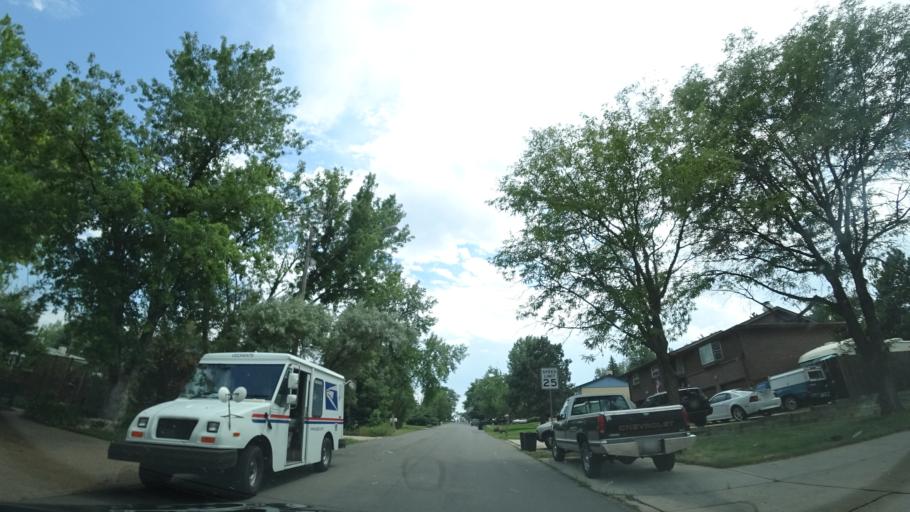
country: US
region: Colorado
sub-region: Jefferson County
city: Lakewood
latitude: 39.6992
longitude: -105.0774
